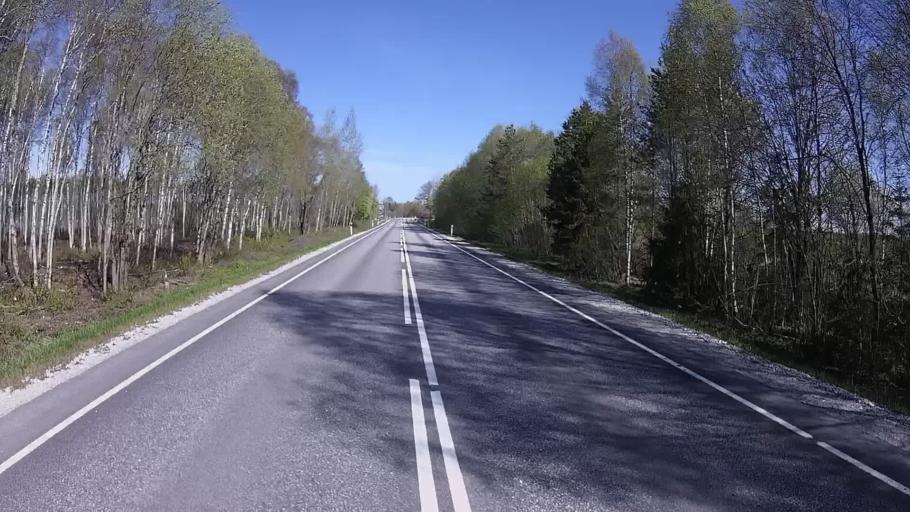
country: EE
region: Raplamaa
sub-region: Jaervakandi vald
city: Jarvakandi
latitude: 58.8719
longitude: 24.7821
